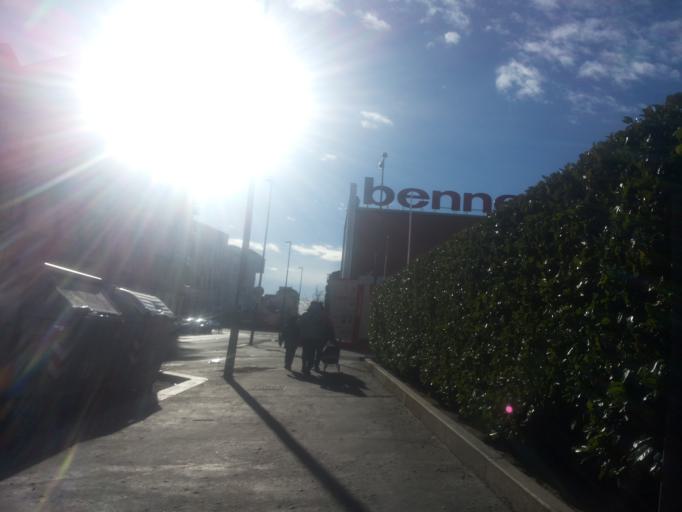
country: IT
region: Piedmont
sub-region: Provincia di Torino
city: Lesna
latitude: 45.0603
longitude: 7.6421
